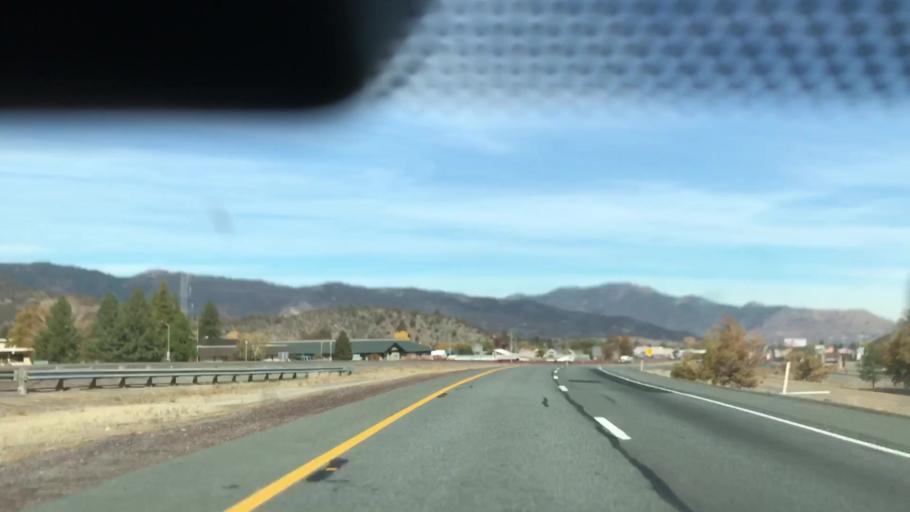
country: US
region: California
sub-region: Siskiyou County
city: Yreka
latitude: 41.7043
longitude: -122.6430
